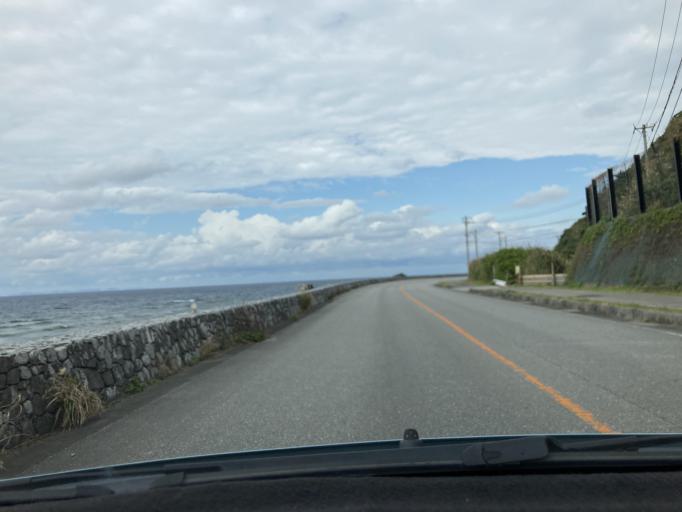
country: JP
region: Okinawa
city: Nago
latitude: 26.7730
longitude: 128.2046
